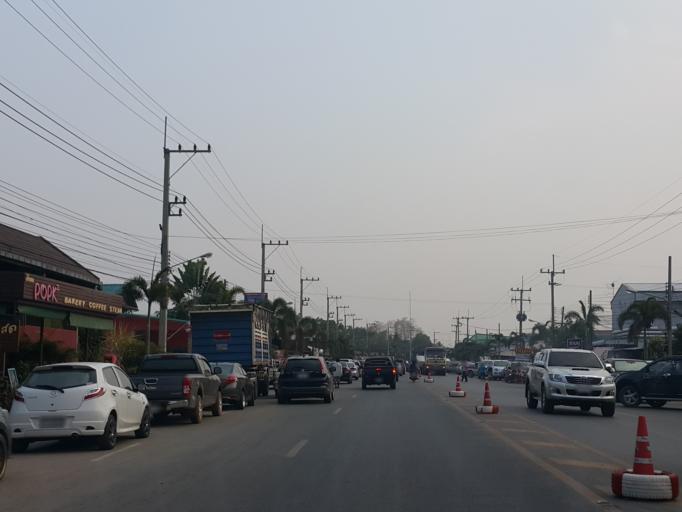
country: TH
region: Uthai Thani
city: Huai Khot
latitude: 15.1816
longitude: 99.6971
